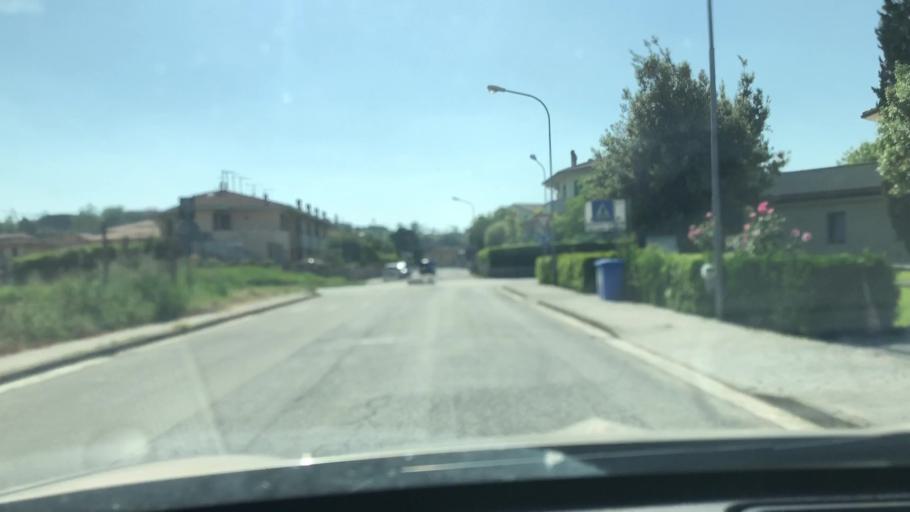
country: IT
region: Tuscany
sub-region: Province of Pisa
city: Capannoli
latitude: 43.5911
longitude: 10.6744
